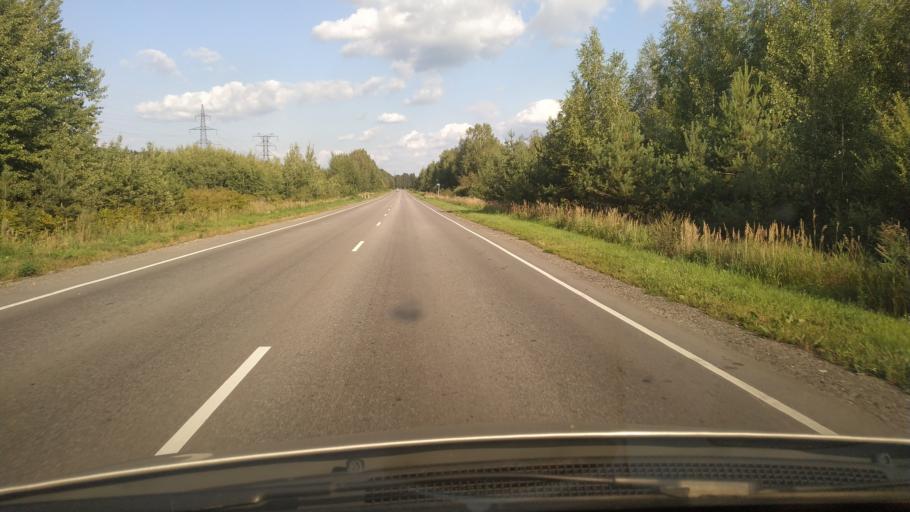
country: RU
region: Moskovskaya
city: Vereya
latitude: 55.7076
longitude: 39.1335
